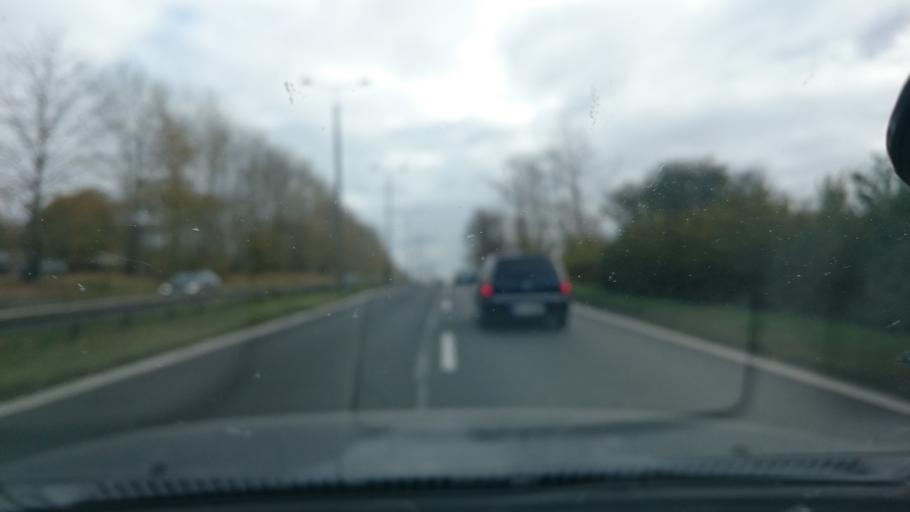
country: PL
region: Silesian Voivodeship
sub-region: Powiat bedzinski
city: Bedzin
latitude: 50.3012
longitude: 19.1518
